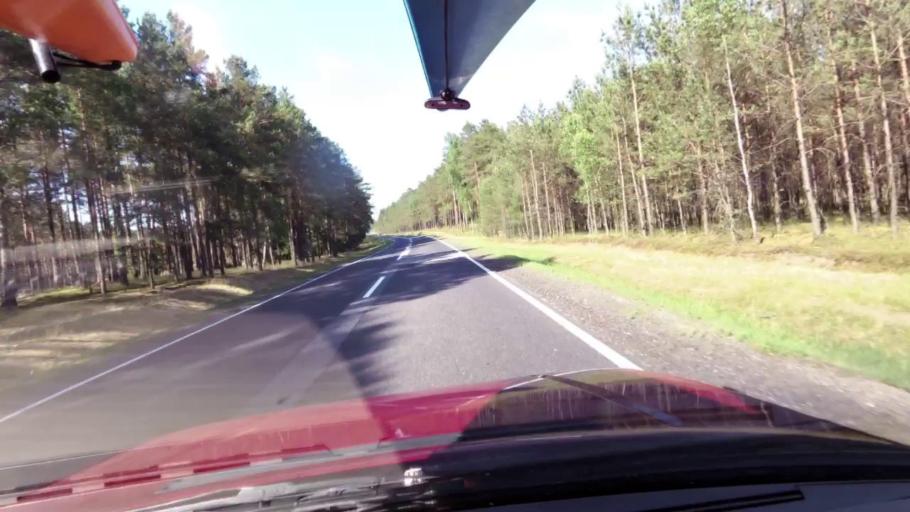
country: PL
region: Pomeranian Voivodeship
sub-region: Powiat bytowski
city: Trzebielino
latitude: 54.1709
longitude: 17.0632
